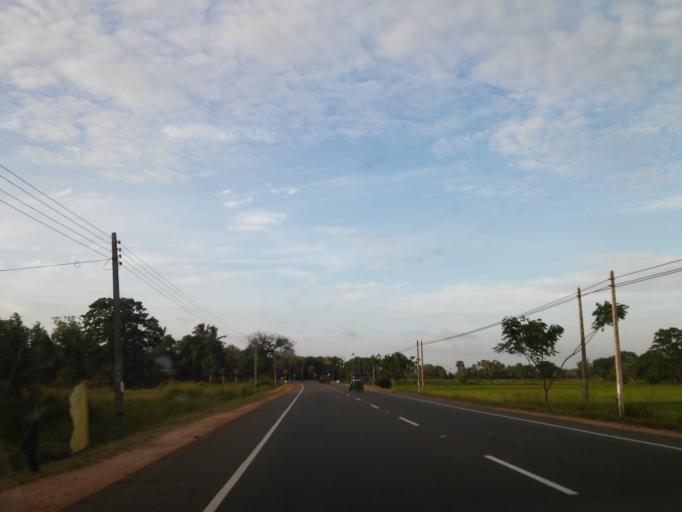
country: LK
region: North Central
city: Anuradhapura
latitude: 8.1998
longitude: 80.5235
